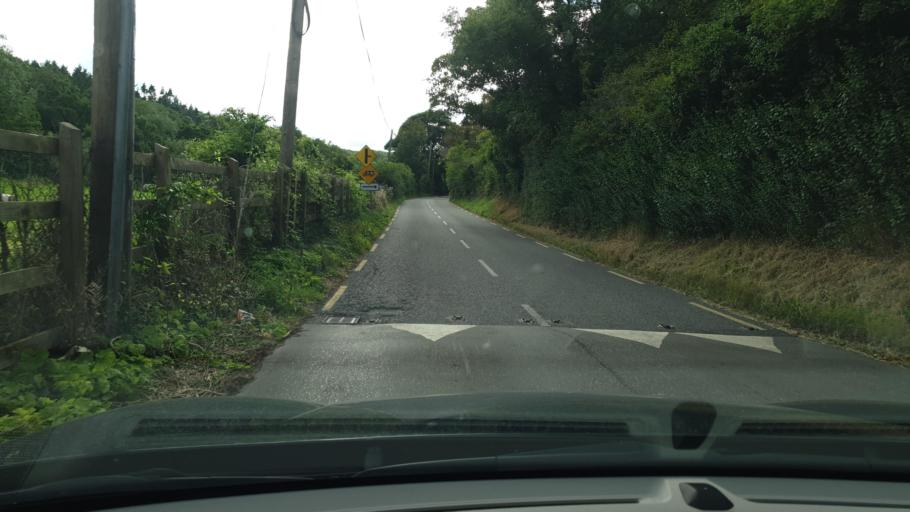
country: IE
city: Palmerstown
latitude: 53.3614
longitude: -6.3917
